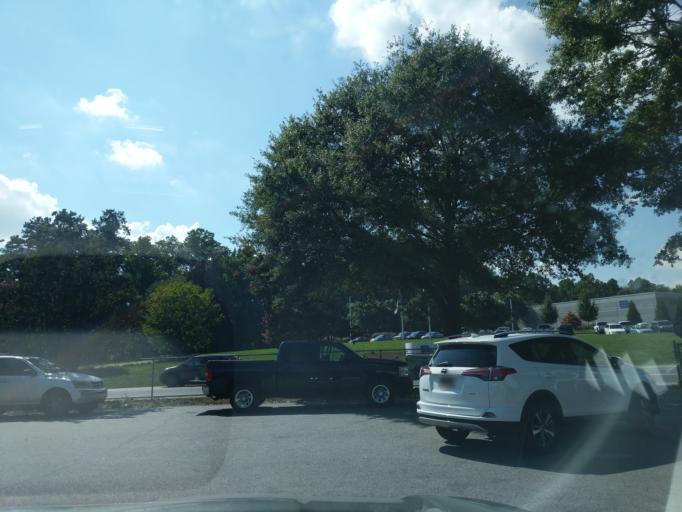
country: US
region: South Carolina
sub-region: Spartanburg County
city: Wellford
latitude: 34.8916
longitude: -82.1010
